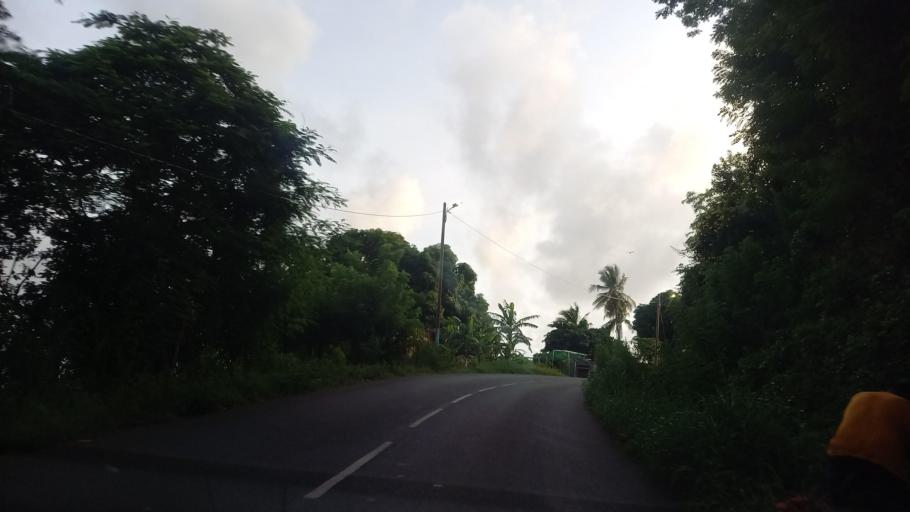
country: YT
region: M'Tsangamouji
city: M'Tsangamouji
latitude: -12.7657
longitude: 45.0794
